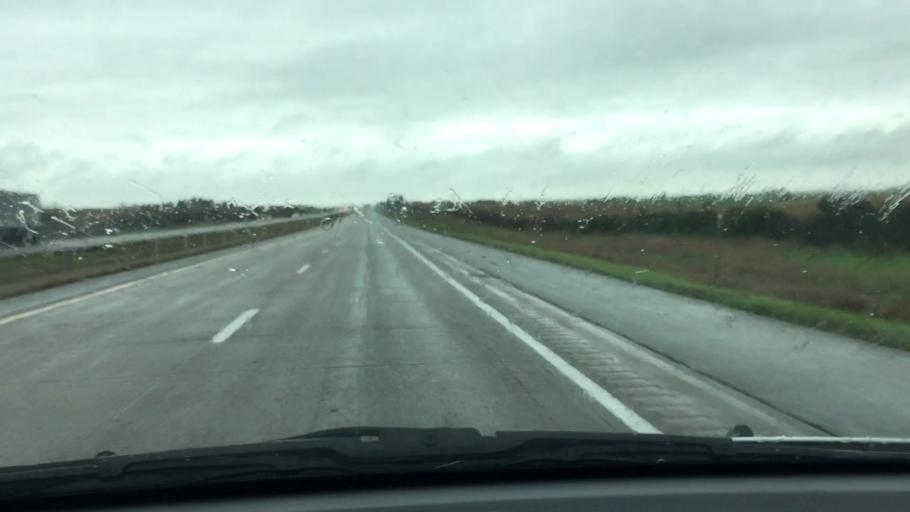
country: US
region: Iowa
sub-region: Poweshiek County
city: Brooklyn
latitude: 41.6953
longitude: -92.4599
